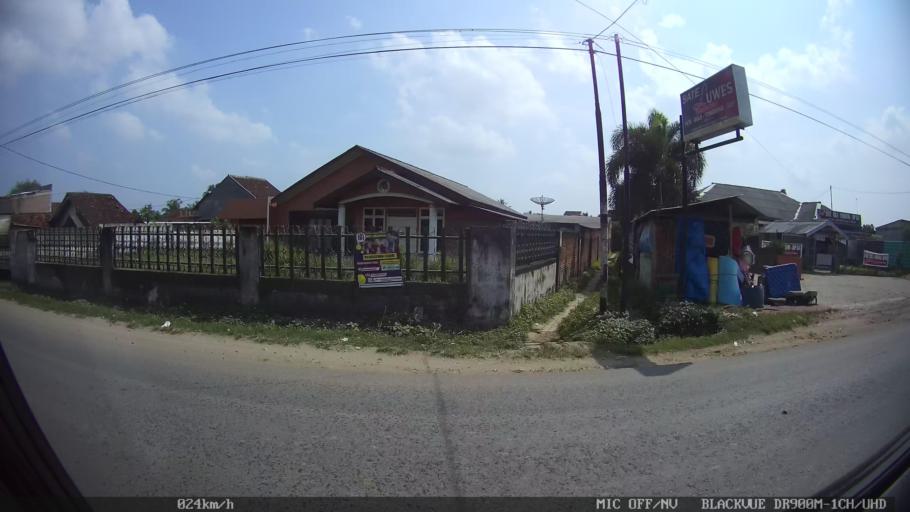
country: ID
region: Lampung
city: Pringsewu
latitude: -5.3602
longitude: 104.9939
